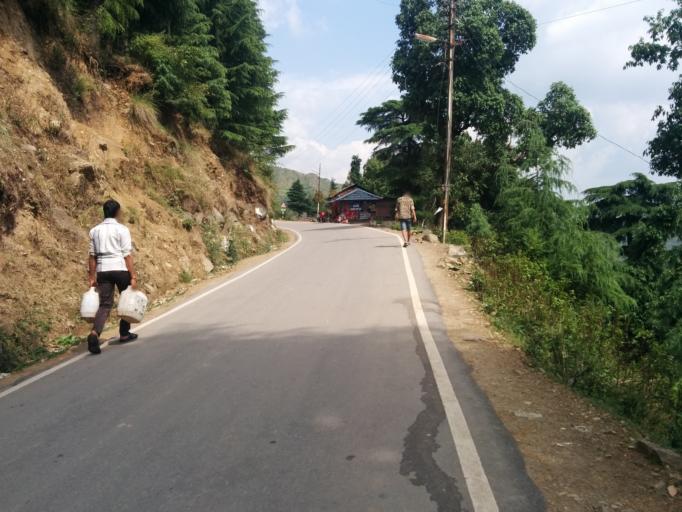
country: IN
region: Himachal Pradesh
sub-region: Kangra
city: Dharmsala
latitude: 32.2394
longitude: 76.3305
